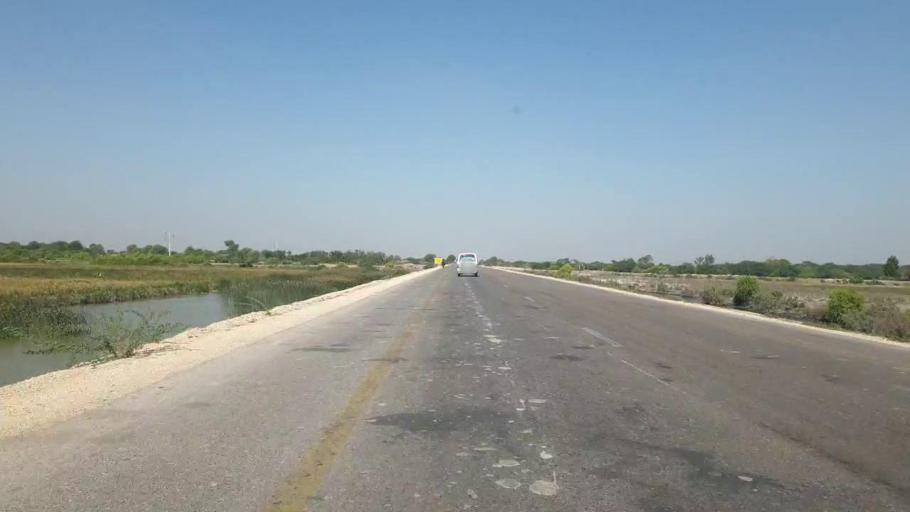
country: PK
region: Sindh
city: Talhar
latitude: 24.8265
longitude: 68.8159
